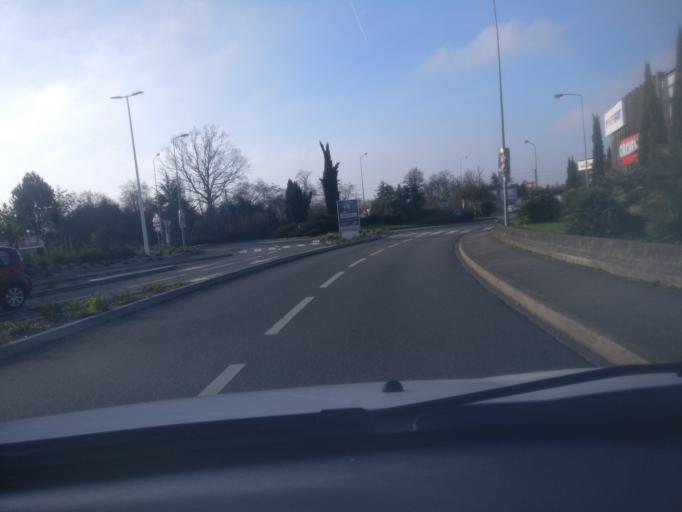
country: FR
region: Pays de la Loire
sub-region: Departement de la Loire-Atlantique
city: Vertou
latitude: 47.1873
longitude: -1.4710
